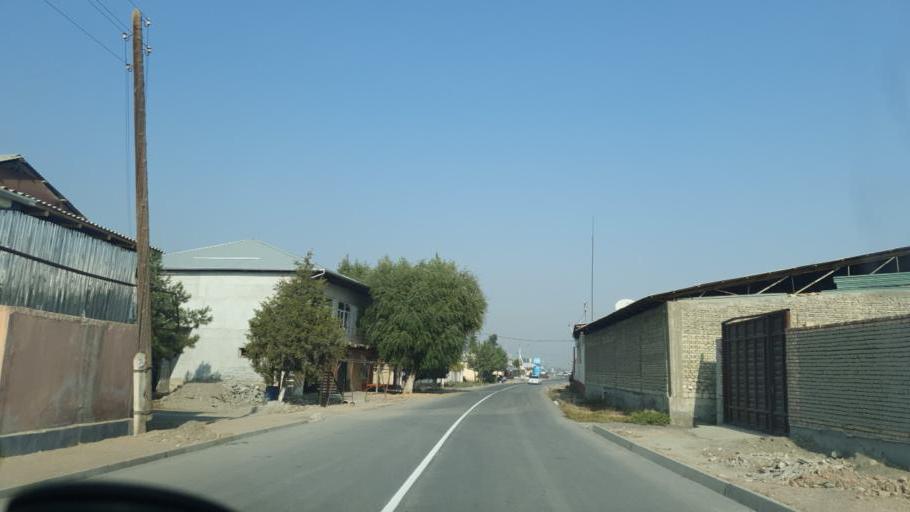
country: UZ
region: Fergana
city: Qo`qon
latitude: 40.5867
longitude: 70.9057
